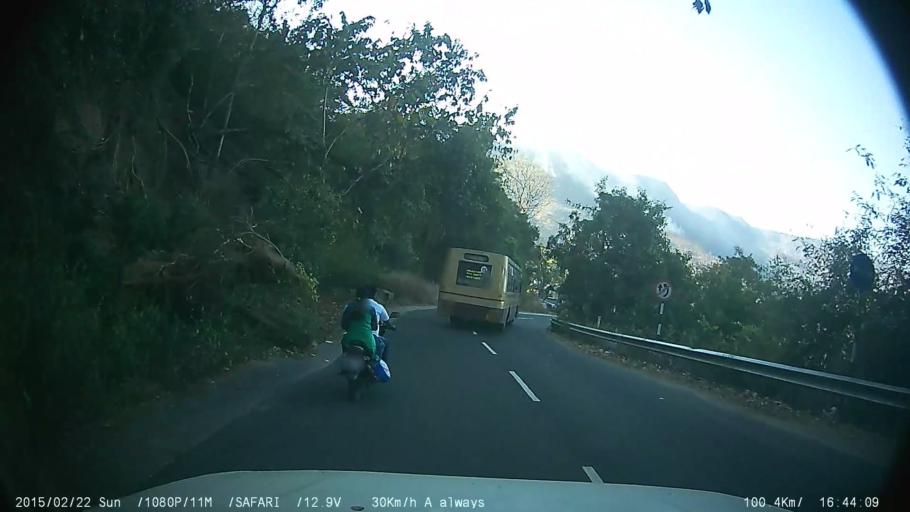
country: IN
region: Tamil Nadu
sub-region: Theni
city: Gudalur
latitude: 9.6216
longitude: 77.1892
